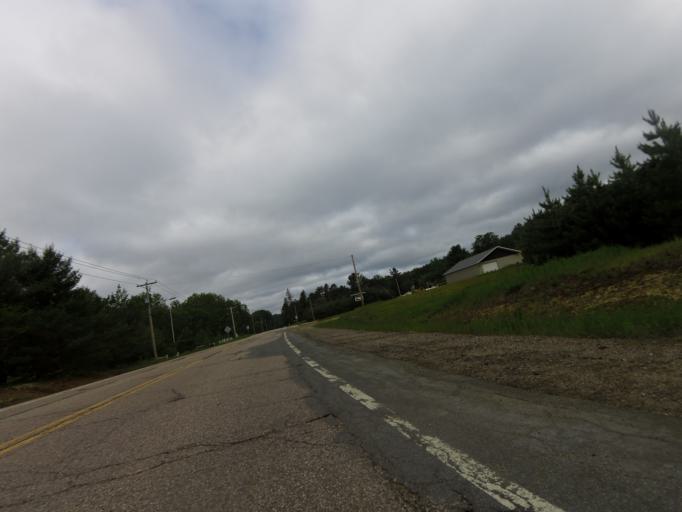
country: CA
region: Quebec
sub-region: Outaouais
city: Shawville
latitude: 45.8379
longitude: -76.4459
